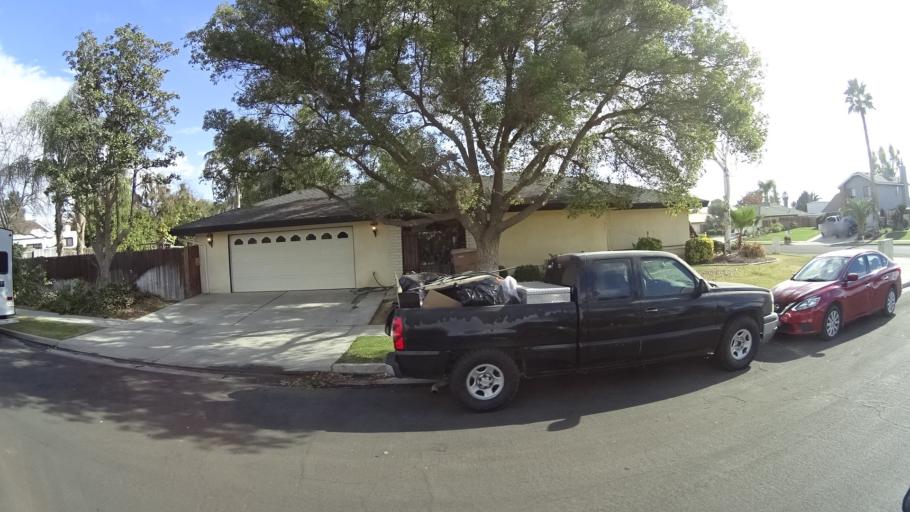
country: US
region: California
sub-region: Kern County
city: Greenacres
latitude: 35.4246
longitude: -119.0783
